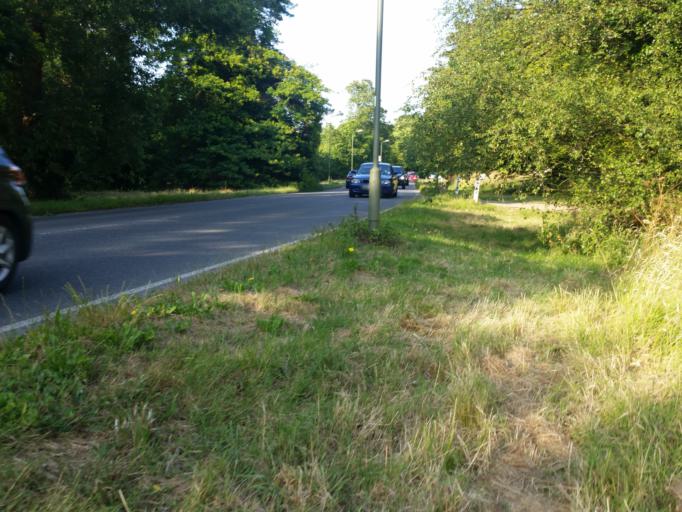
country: GB
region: England
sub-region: Greater London
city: High Barnet
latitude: 51.6314
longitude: -0.2242
